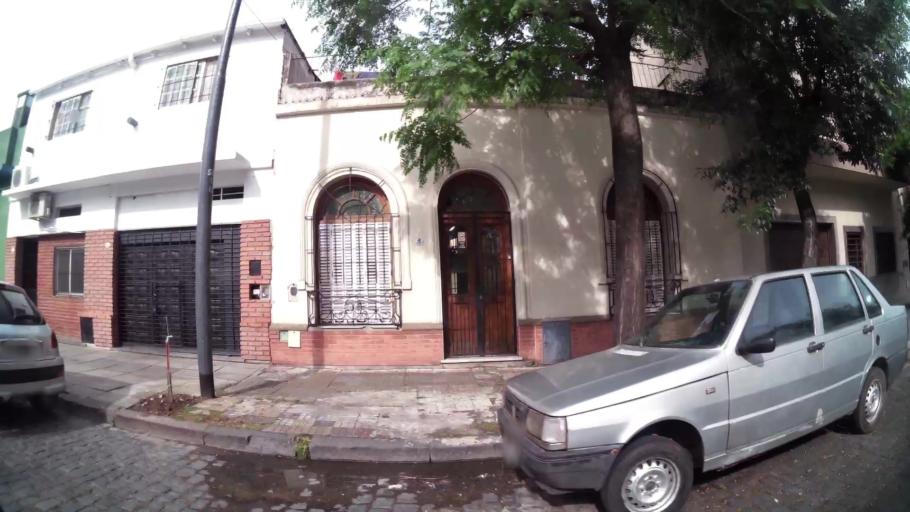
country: AR
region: Buenos Aires F.D.
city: Buenos Aires
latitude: -34.6407
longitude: -58.4197
